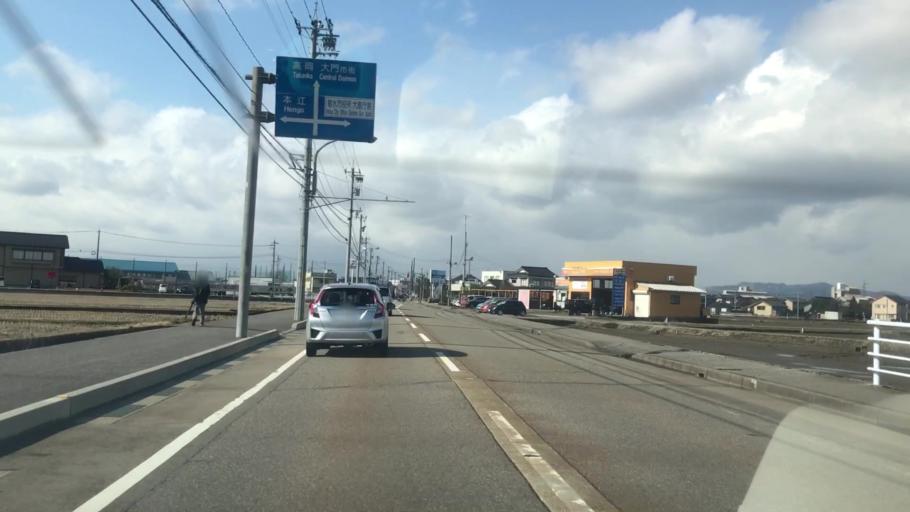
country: JP
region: Toyama
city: Takaoka
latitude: 36.7272
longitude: 137.0617
